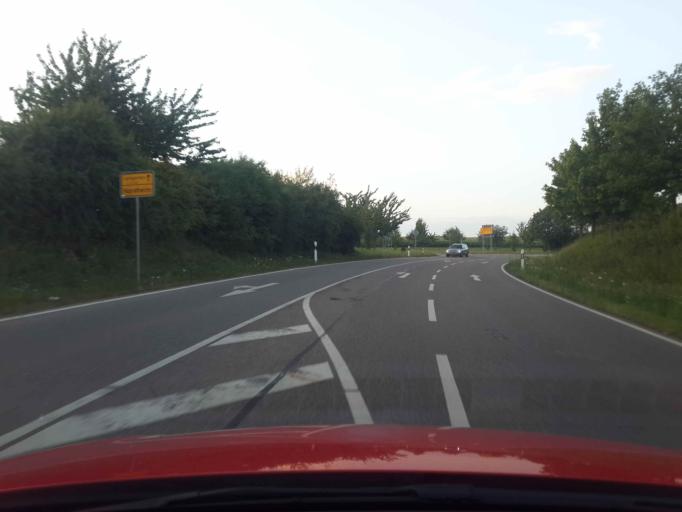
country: DE
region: Baden-Wuerttemberg
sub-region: Regierungsbezirk Stuttgart
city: Nordheim
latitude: 49.1127
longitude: 9.1290
